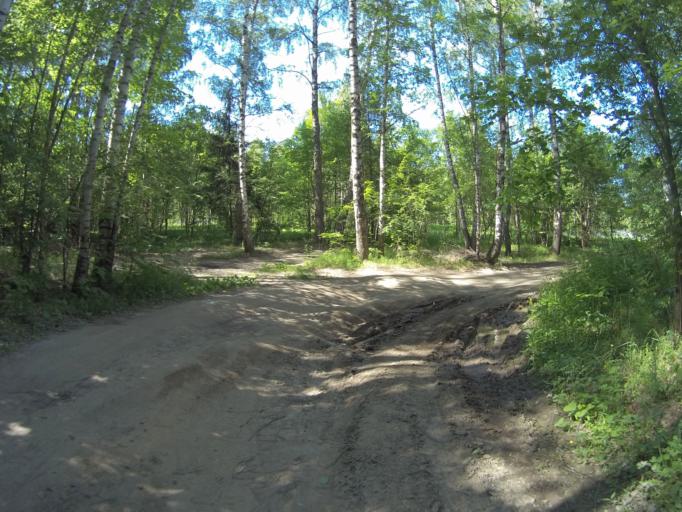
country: RU
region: Vladimir
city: Raduzhnyy
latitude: 55.9904
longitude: 40.3717
